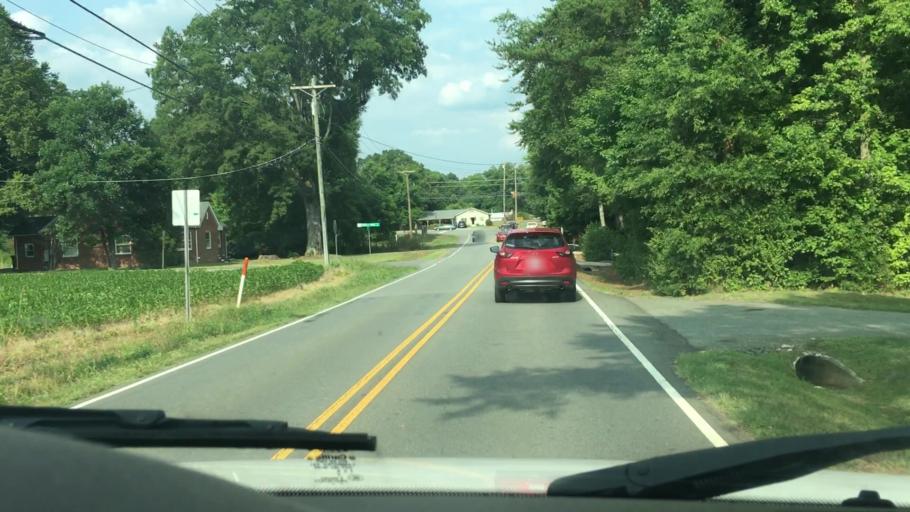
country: US
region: North Carolina
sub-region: Mecklenburg County
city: Huntersville
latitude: 35.4262
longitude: -80.8447
